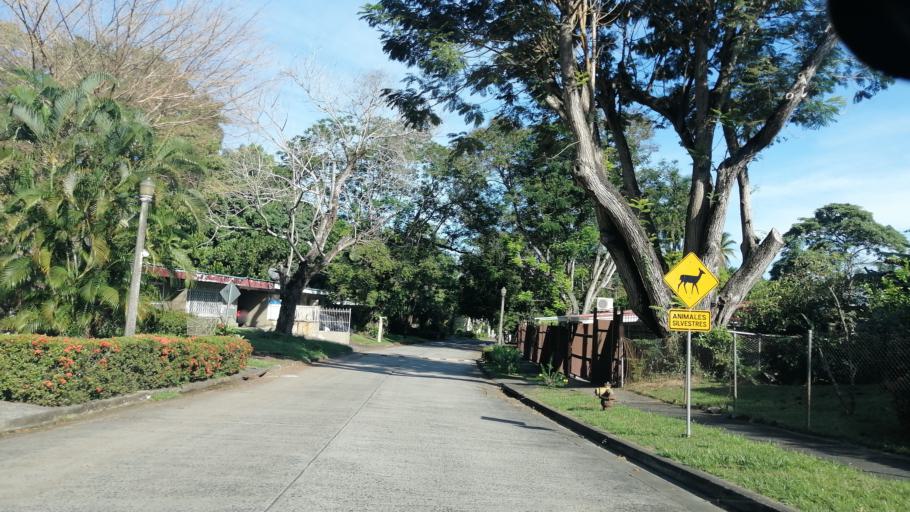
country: PA
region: Panama
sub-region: Distrito de Panama
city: Ancon
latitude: 8.9635
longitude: -79.5469
